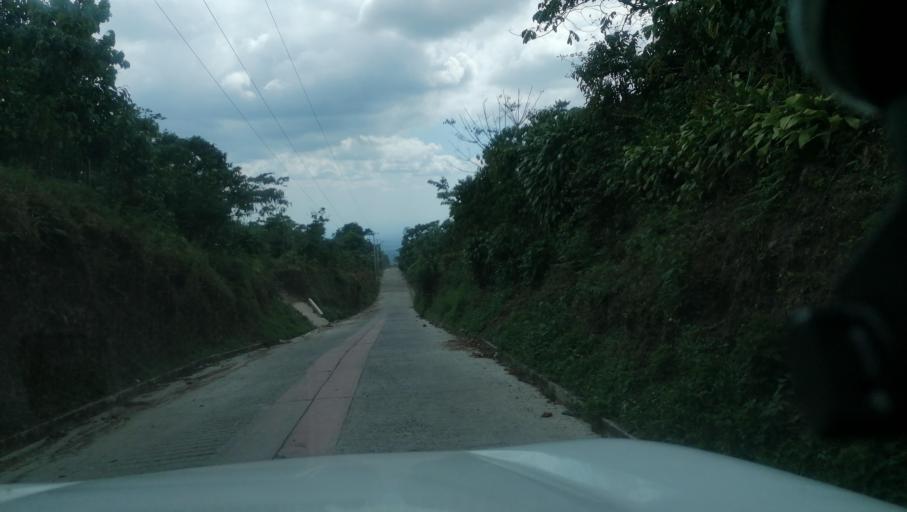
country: MX
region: Chiapas
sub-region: Cacahoatan
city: Benito Juarez
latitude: 15.0720
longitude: -92.1511
